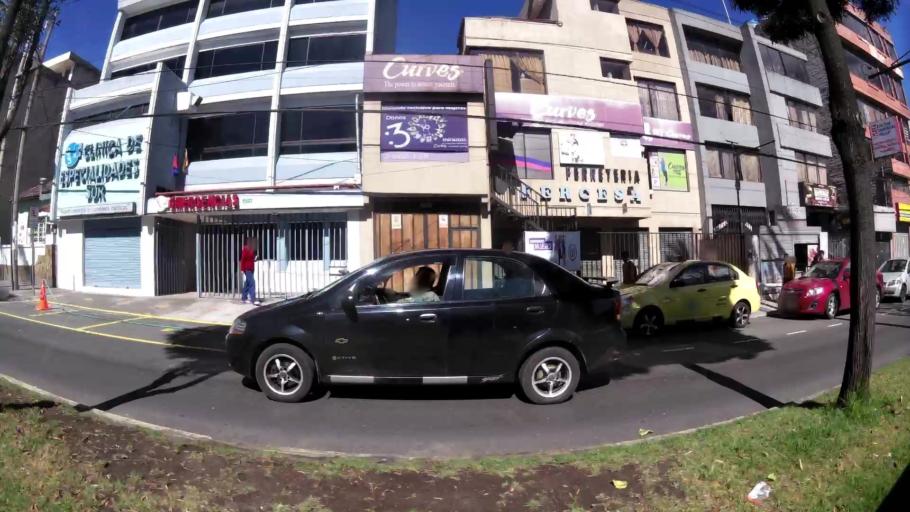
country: EC
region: Pichincha
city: Quito
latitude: -0.2412
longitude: -78.5217
